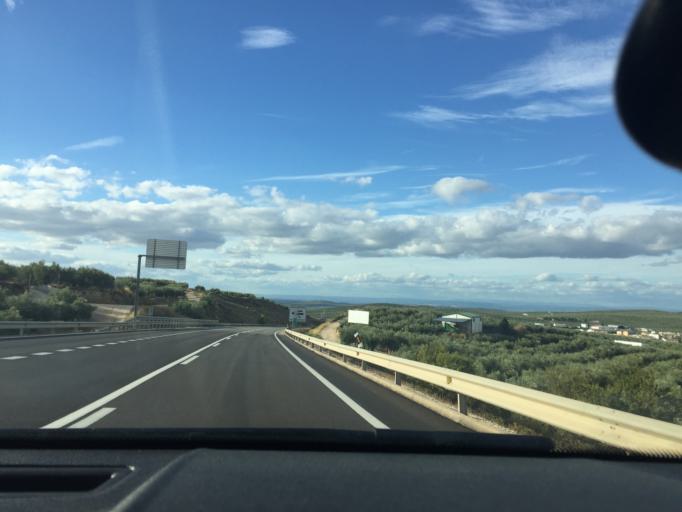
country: ES
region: Andalusia
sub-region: Provincia de Jaen
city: Torredonjimeno
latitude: 37.7580
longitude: -3.9634
